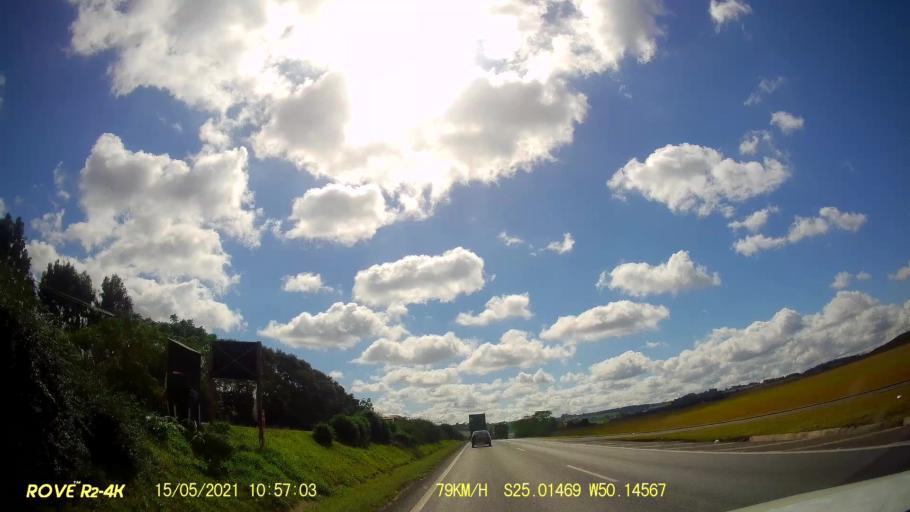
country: BR
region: Parana
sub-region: Carambei
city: Carambei
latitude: -25.0152
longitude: -50.1460
